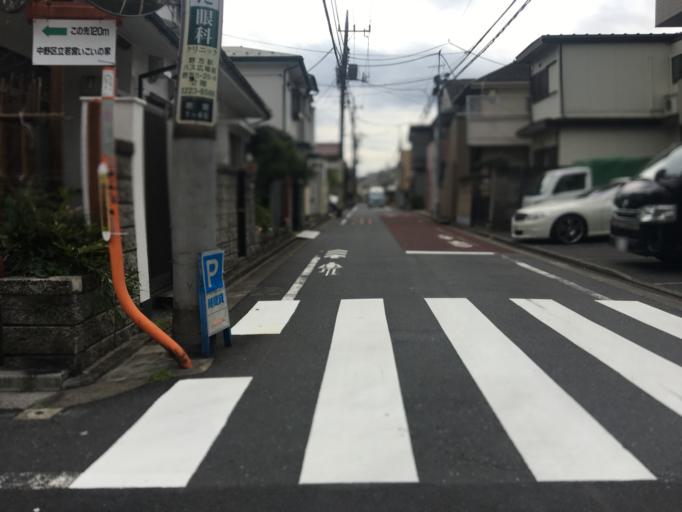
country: JP
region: Tokyo
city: Tokyo
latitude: 35.7209
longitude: 139.6471
